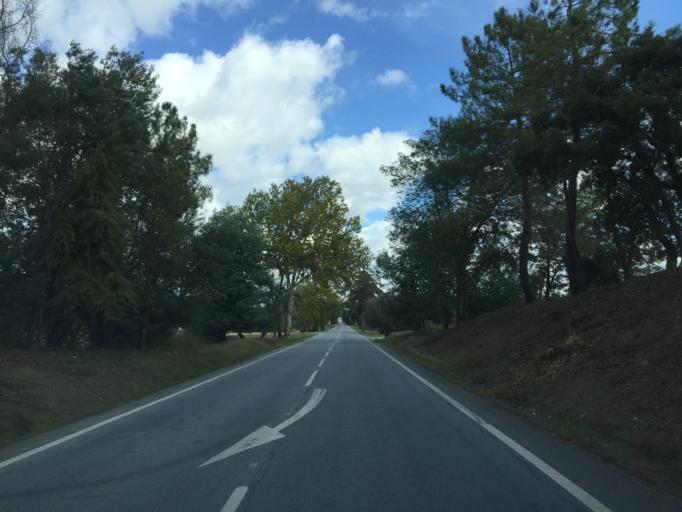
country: PT
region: Portalegre
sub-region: Ponte de Sor
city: Santo Andre
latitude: 39.0923
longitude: -8.1577
